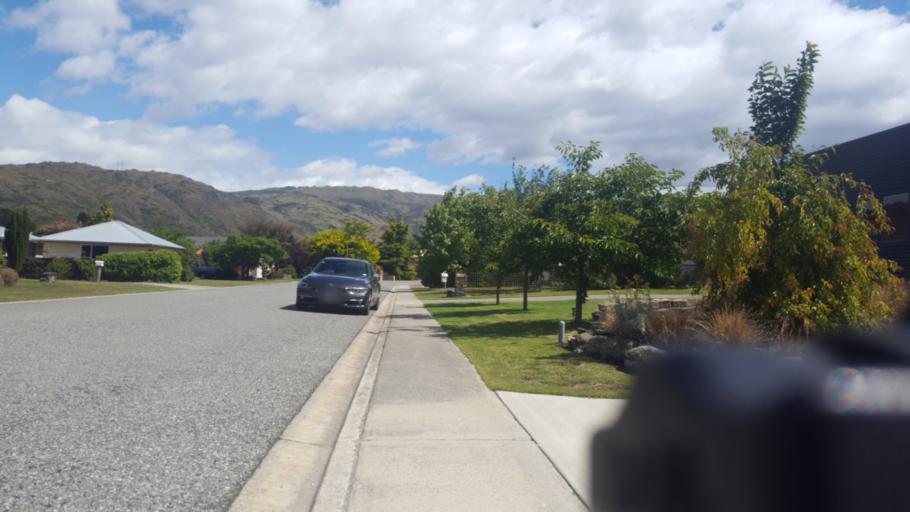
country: NZ
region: Otago
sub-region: Queenstown-Lakes District
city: Wanaka
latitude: -45.1951
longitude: 169.3284
